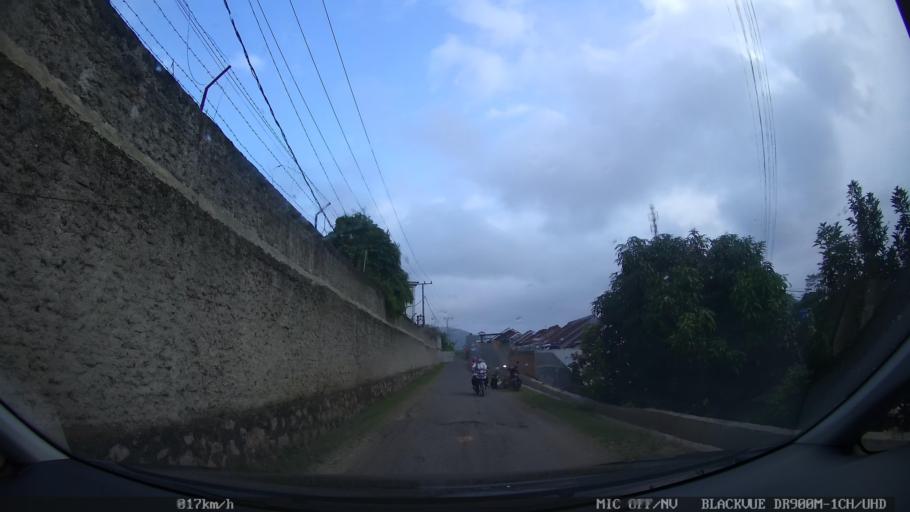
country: ID
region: Lampung
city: Bandarlampung
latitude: -5.4147
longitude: 105.2854
